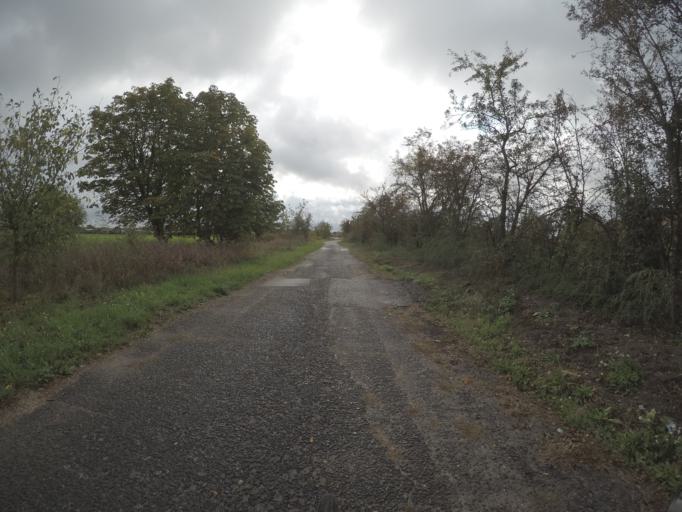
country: DE
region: Berlin
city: Blankenfelde
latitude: 52.6633
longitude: 13.3885
